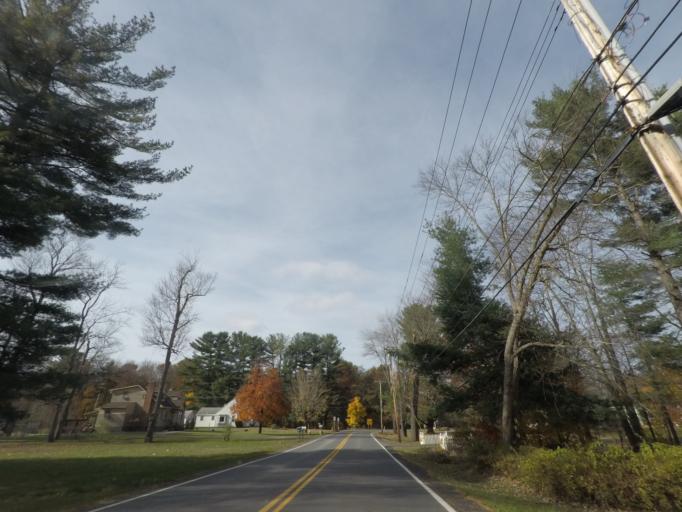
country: US
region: New York
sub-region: Schenectady County
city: Rotterdam
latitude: 42.7547
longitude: -73.9586
